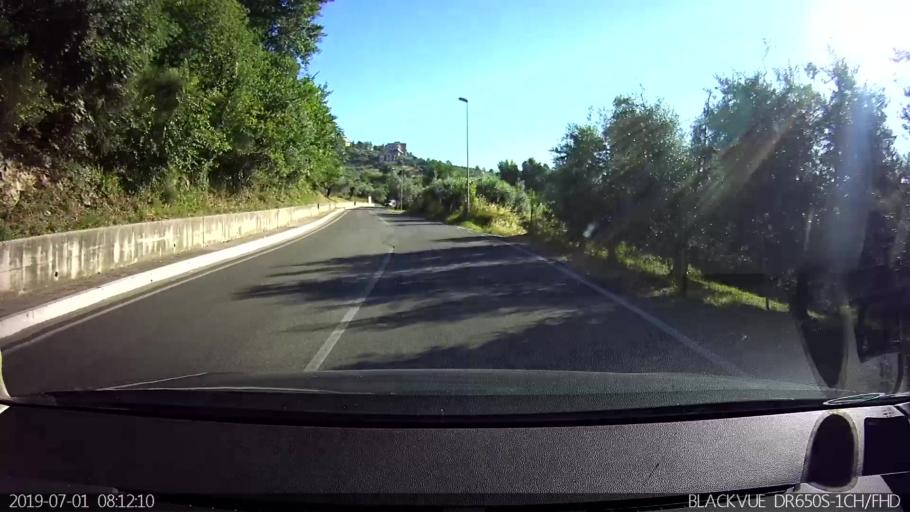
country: IT
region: Latium
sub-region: Provincia di Frosinone
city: Veroli
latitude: 41.6830
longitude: 13.4174
